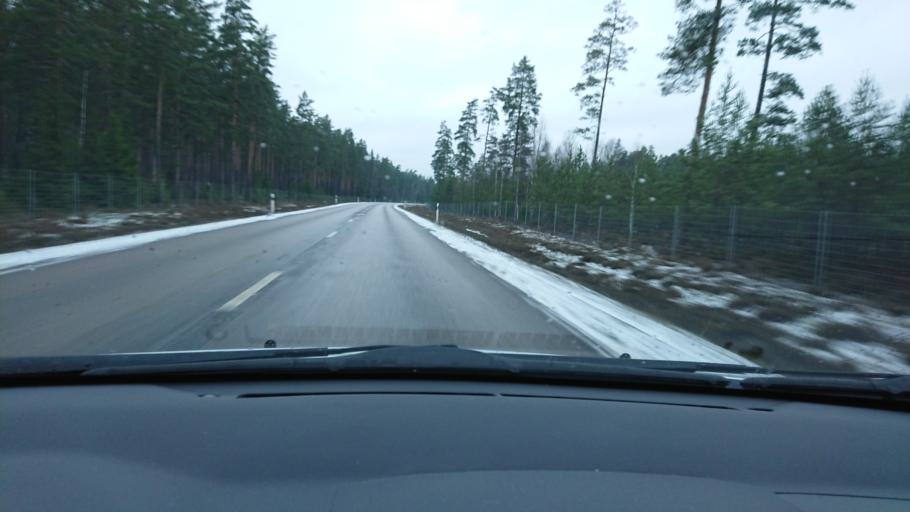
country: SE
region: Kalmar
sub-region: Vimmerby Kommun
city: Vimmerby
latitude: 57.6216
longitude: 15.8421
